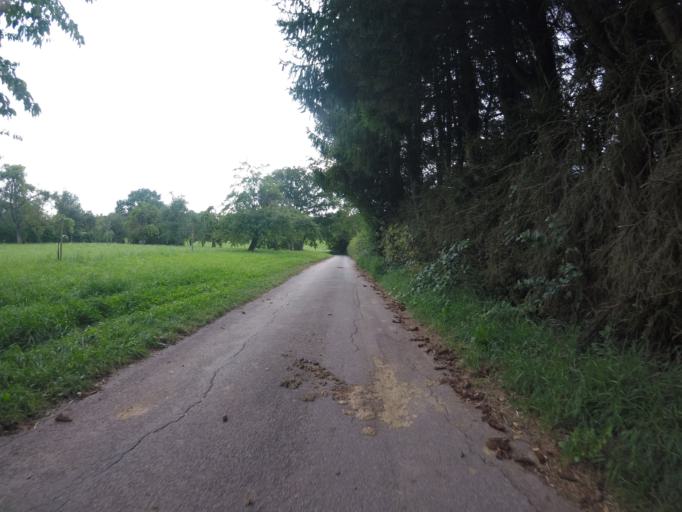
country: DE
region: Baden-Wuerttemberg
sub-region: Regierungsbezirk Stuttgart
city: Backnang
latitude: 48.9416
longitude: 9.4494
